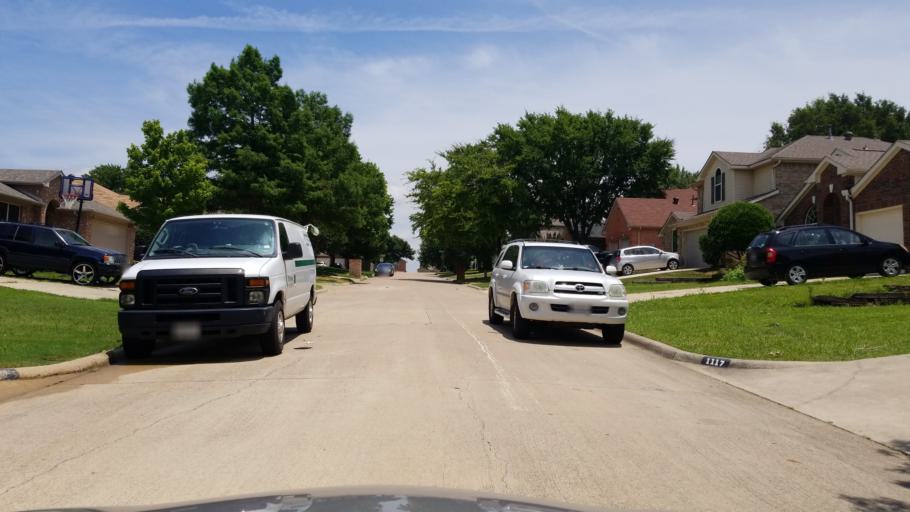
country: US
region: Texas
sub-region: Dallas County
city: Grand Prairie
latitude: 32.6774
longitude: -96.9922
